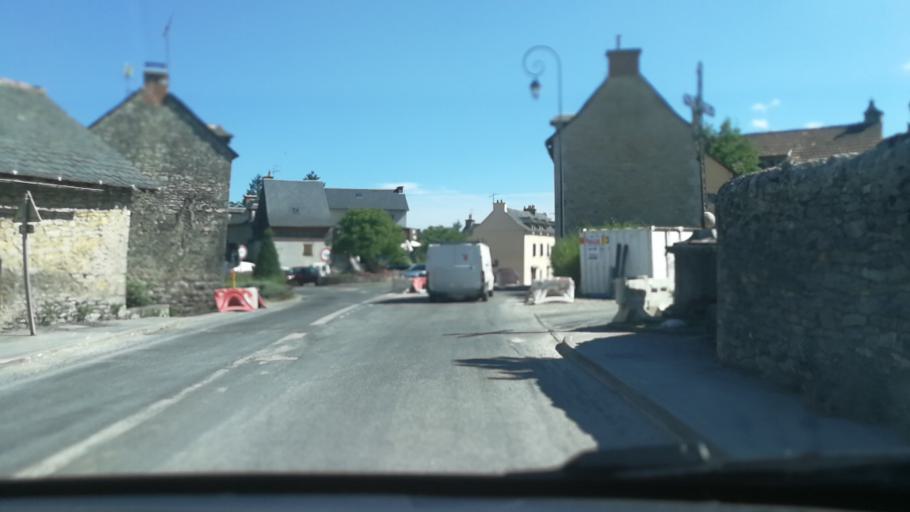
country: FR
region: Midi-Pyrenees
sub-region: Departement de l'Aveyron
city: Sebazac-Concoures
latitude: 44.4050
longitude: 2.5995
